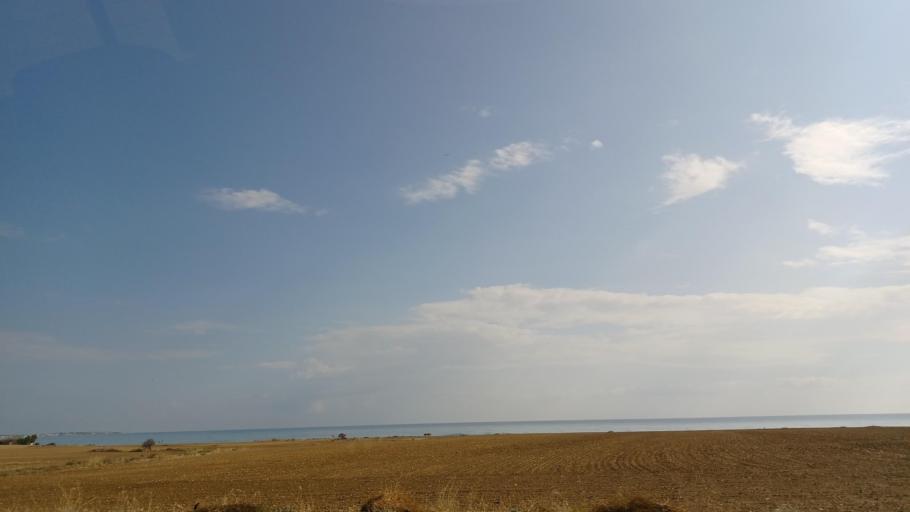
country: CY
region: Larnaka
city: Tersefanou
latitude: 34.8098
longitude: 33.5308
